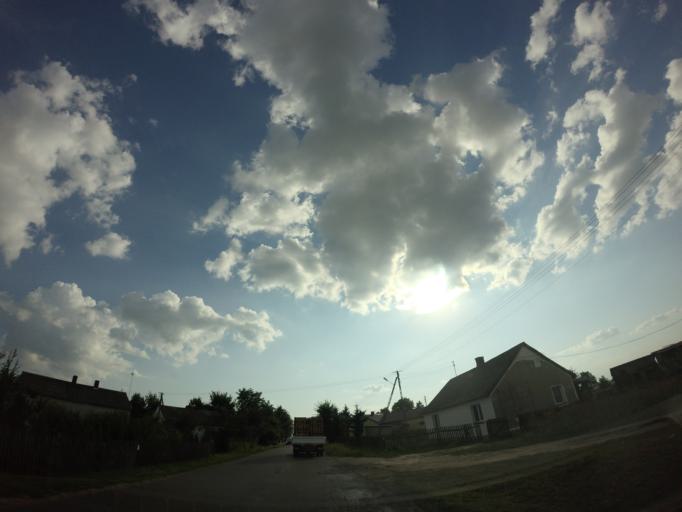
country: PL
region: Lublin Voivodeship
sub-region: Powiat lukowski
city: Adamow
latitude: 51.7587
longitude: 22.2809
